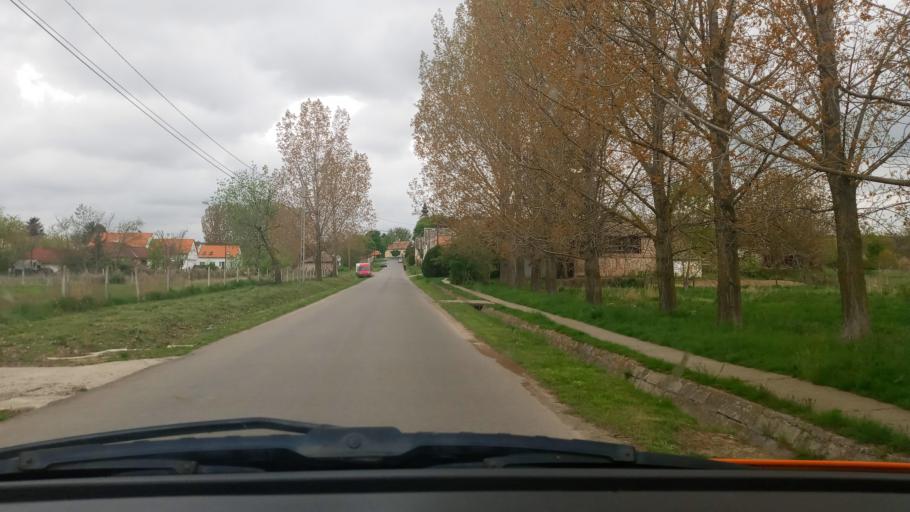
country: HU
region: Baranya
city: Boly
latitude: 45.9931
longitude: 18.5161
